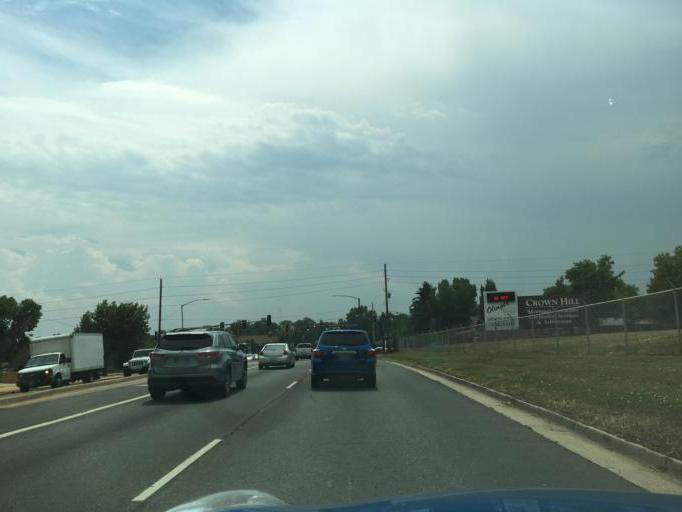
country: US
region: Colorado
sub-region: Jefferson County
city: Wheat Ridge
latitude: 39.7558
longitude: -105.0815
